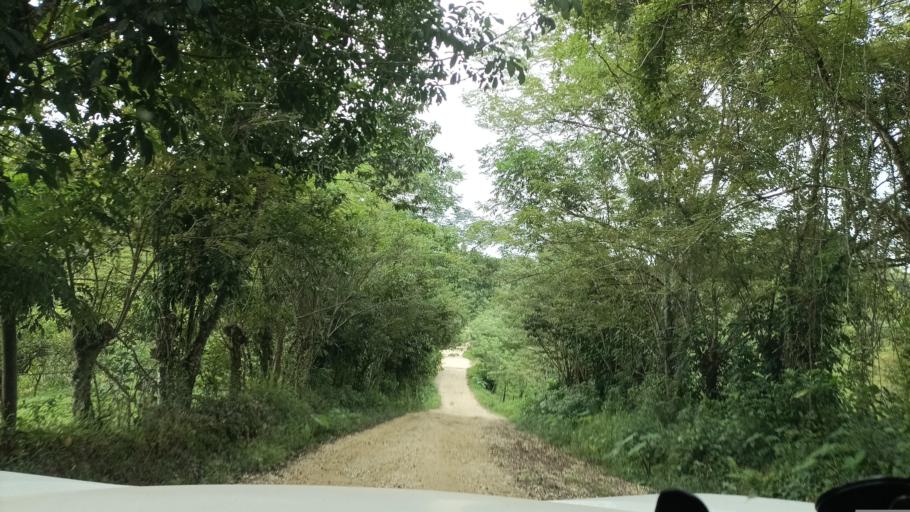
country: MX
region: Veracruz
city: Hidalgotitlan
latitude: 17.5774
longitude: -94.4225
